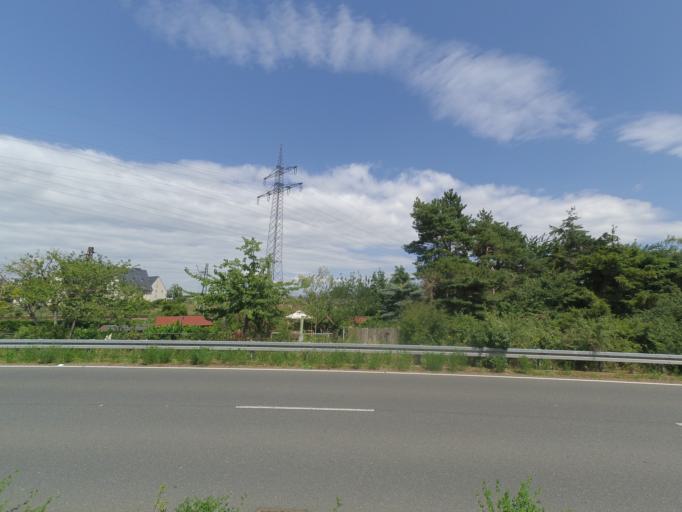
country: DE
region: Baden-Wuerttemberg
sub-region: Karlsruhe Region
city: Schwetzingen
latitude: 49.3999
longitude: 8.5641
